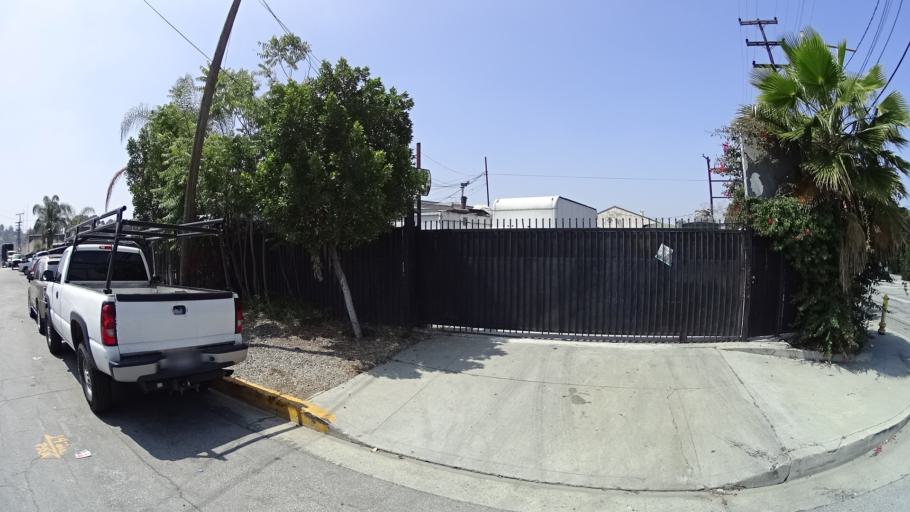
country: US
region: California
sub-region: Los Angeles County
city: Belvedere
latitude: 34.0607
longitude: -118.1800
